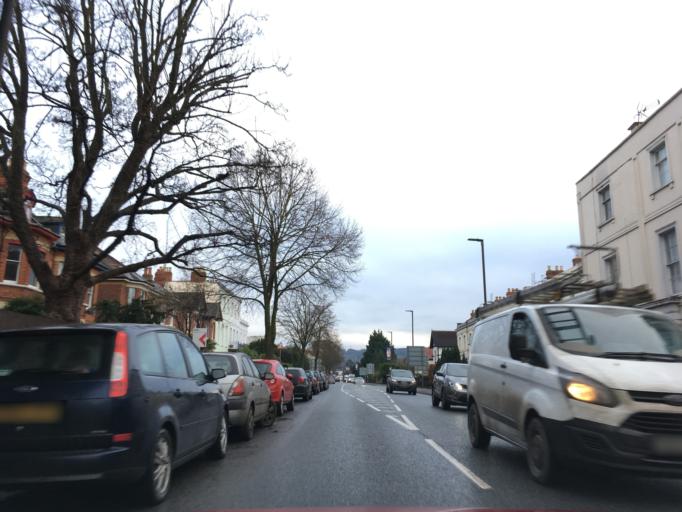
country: GB
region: England
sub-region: Gloucestershire
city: Cheltenham
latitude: 51.8932
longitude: -2.0638
